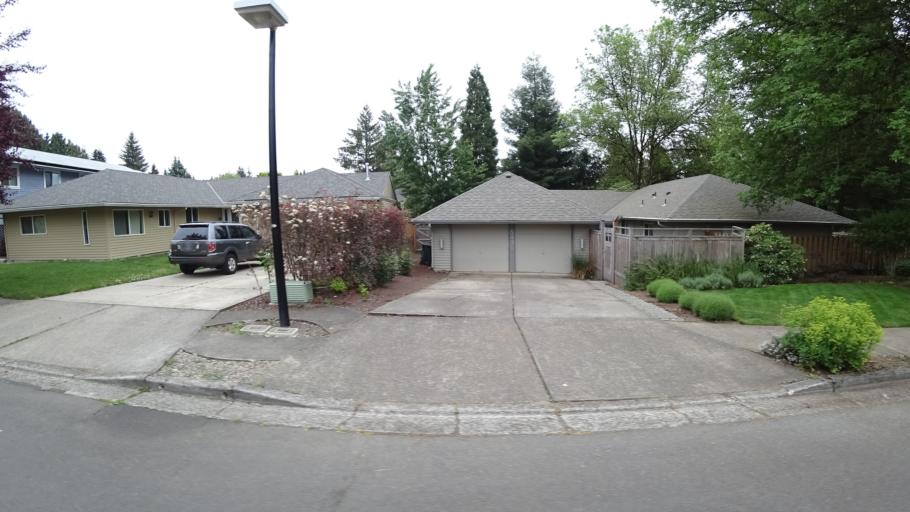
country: US
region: Oregon
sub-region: Washington County
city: Rockcreek
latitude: 45.5590
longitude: -122.8830
